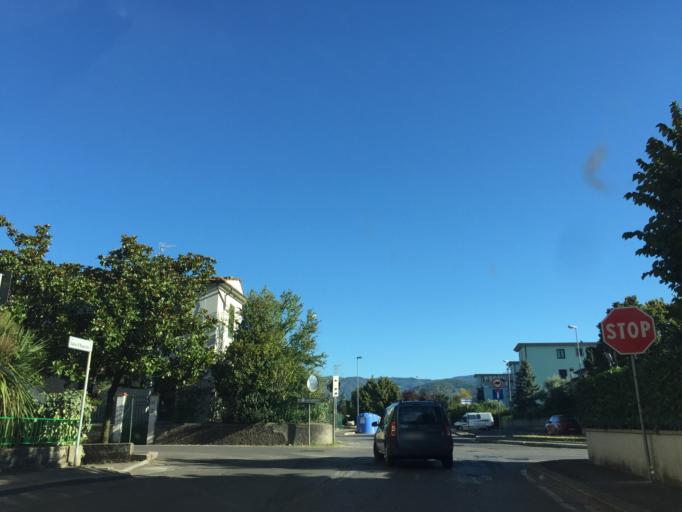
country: IT
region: Tuscany
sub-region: Provincia di Pistoia
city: Pistoia
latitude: 43.9381
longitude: 10.8978
